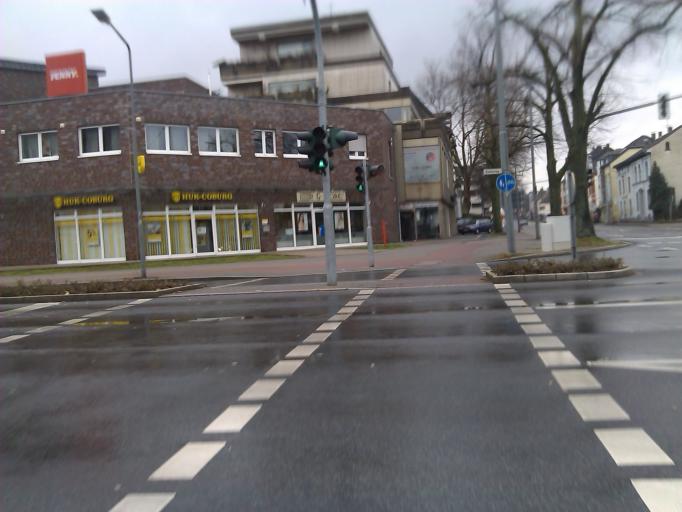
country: DE
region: North Rhine-Westphalia
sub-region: Regierungsbezirk Dusseldorf
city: Ratingen
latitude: 51.2938
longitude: 6.8430
